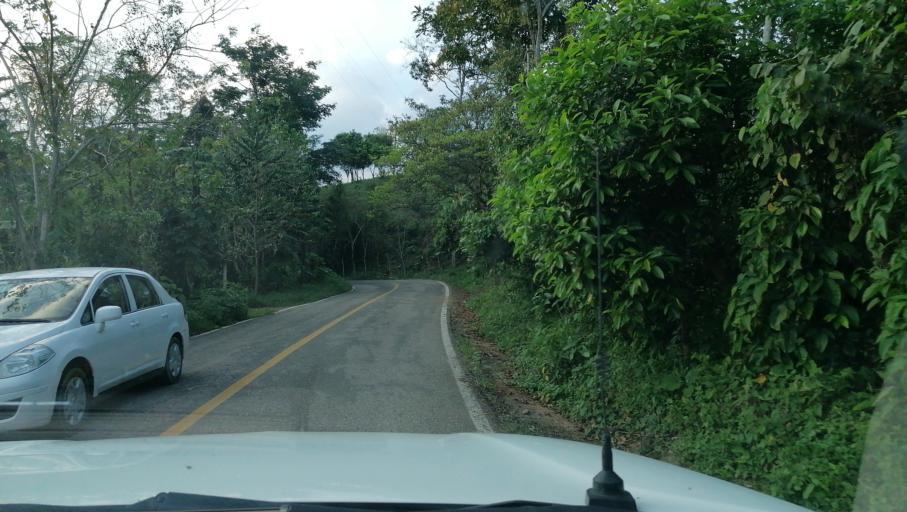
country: MX
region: Chiapas
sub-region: Juarez
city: El Triunfo 1ra. Seccion (Cardona)
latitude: 17.4954
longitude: -93.2439
